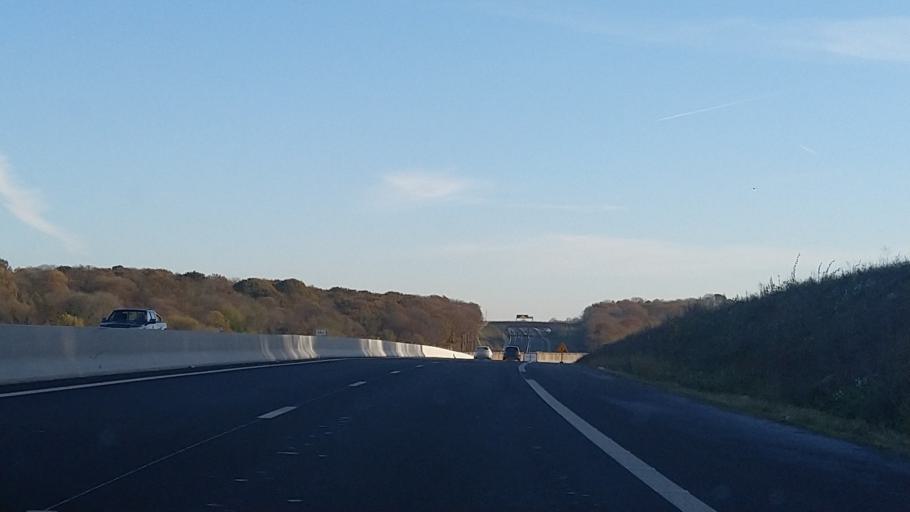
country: FR
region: Ile-de-France
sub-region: Departement du Val-d'Oise
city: Maffliers
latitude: 49.0968
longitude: 2.2956
